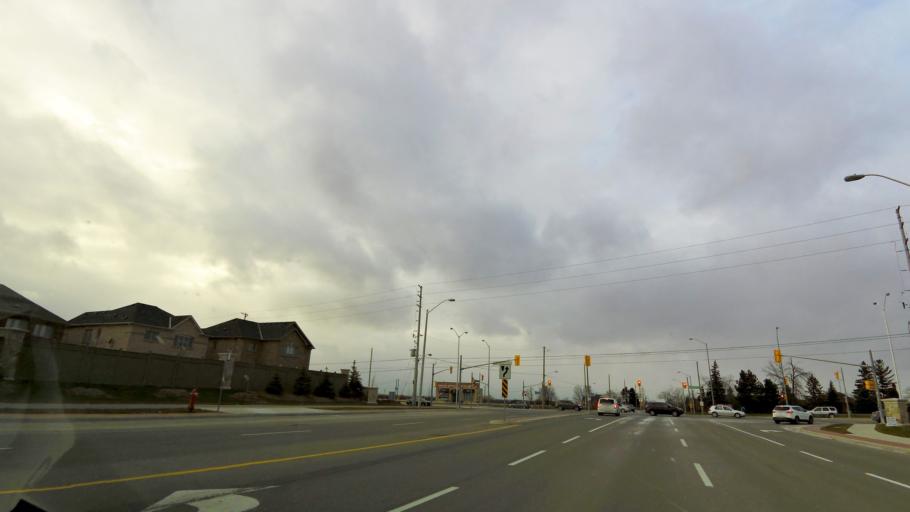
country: CA
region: Ontario
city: Brampton
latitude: 43.8005
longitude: -79.6779
